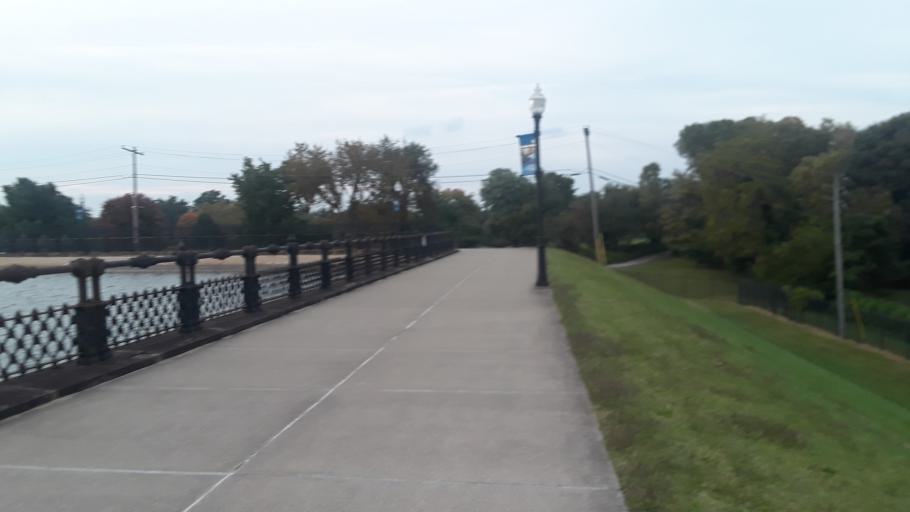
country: US
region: Kentucky
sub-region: Jefferson County
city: Indian Hills
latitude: 38.2580
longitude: -85.6779
